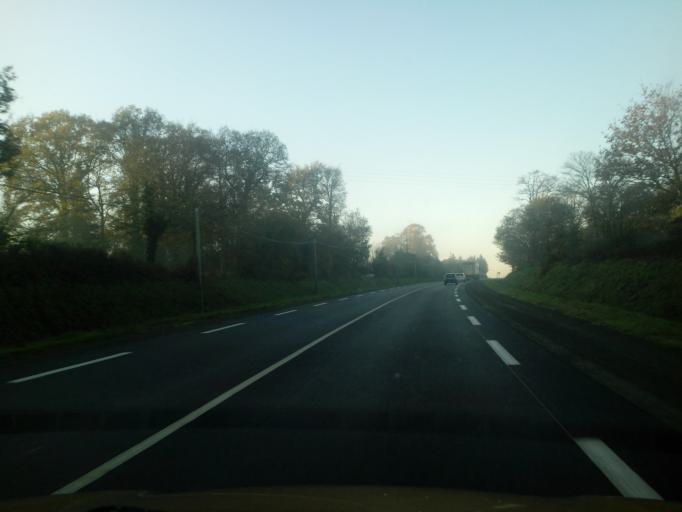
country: FR
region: Brittany
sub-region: Departement du Morbihan
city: Mauron
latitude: 48.0325
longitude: -2.3046
